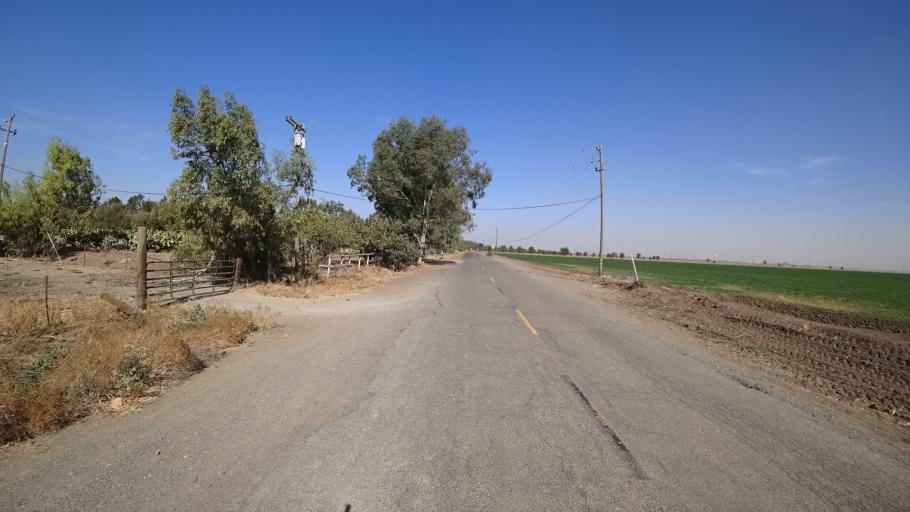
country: US
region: California
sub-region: Yolo County
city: Davis
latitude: 38.4847
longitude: -121.6937
